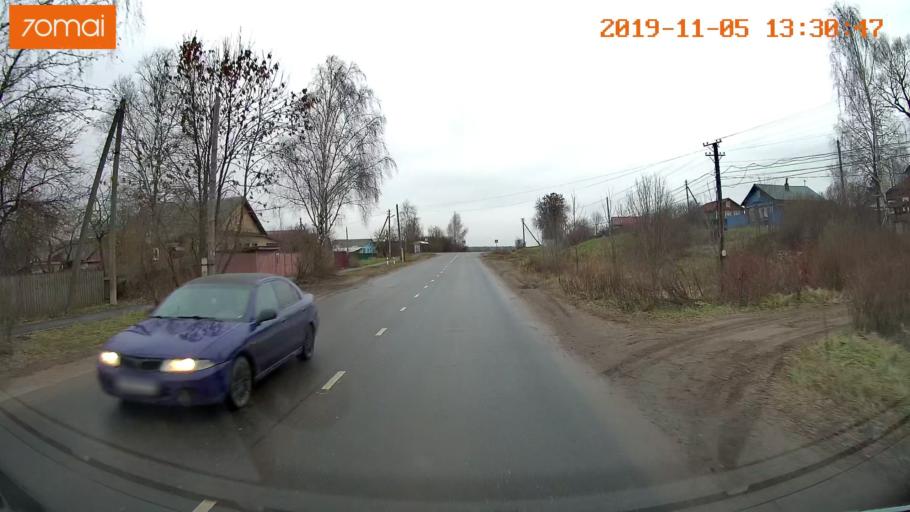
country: RU
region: Ivanovo
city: Shuya
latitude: 56.8694
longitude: 41.3941
